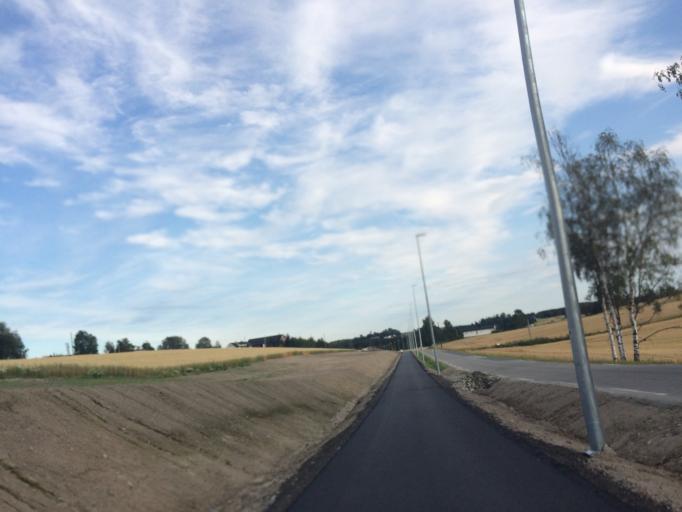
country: NO
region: Akershus
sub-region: Ski
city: Ski
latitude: 59.6923
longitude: 10.8613
